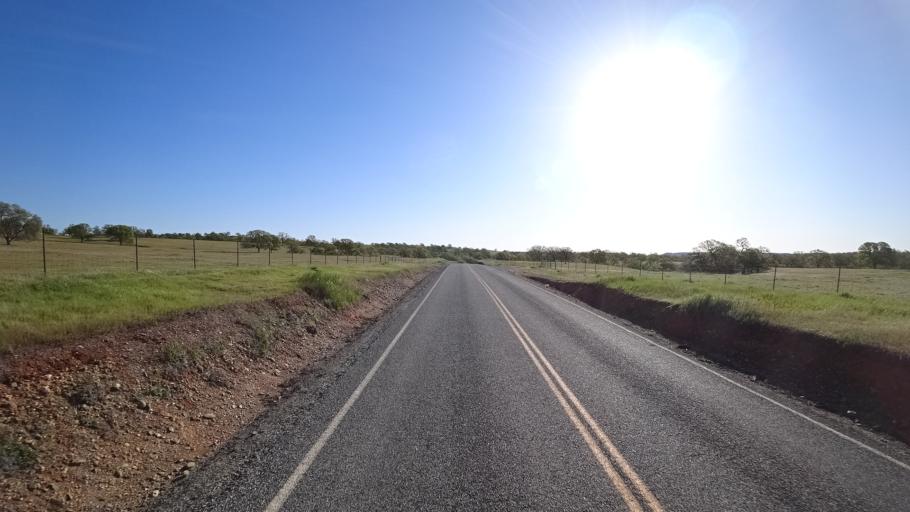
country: US
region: California
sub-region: Tehama County
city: Rancho Tehama Reserve
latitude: 39.8098
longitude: -122.4169
